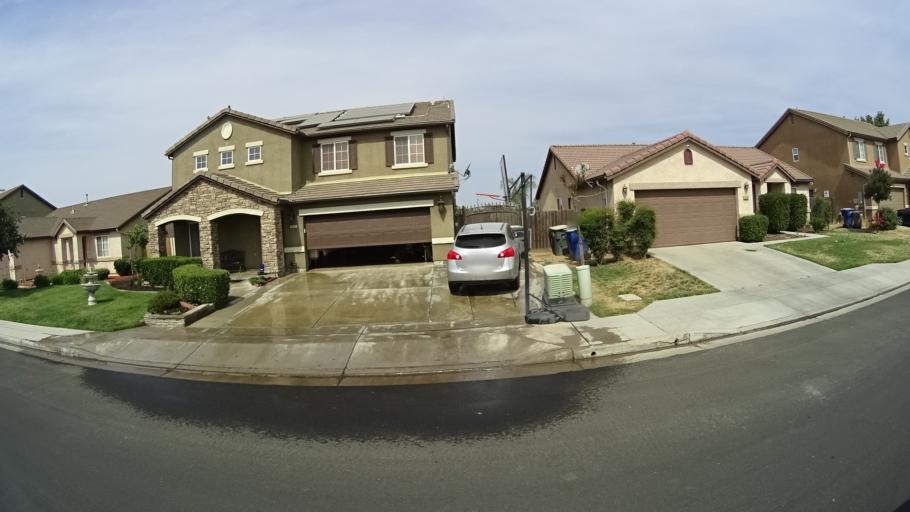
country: US
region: California
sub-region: Fresno County
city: West Park
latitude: 36.7638
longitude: -119.8868
